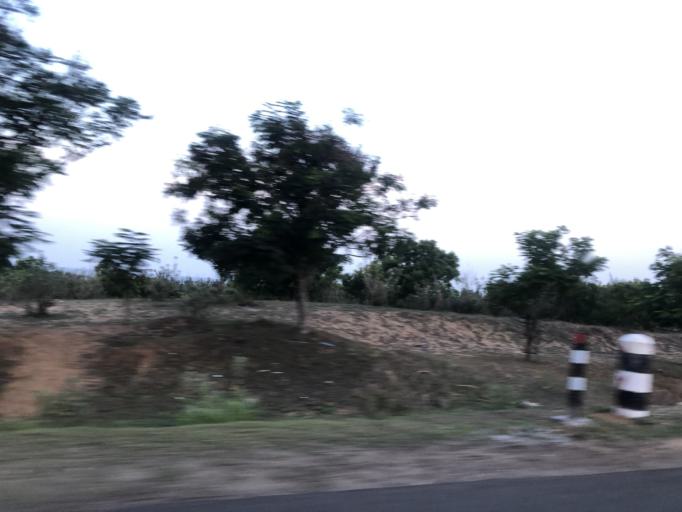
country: IN
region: Tamil Nadu
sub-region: Kancheepuram
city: Mamallapuram
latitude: 12.7577
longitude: 80.2436
